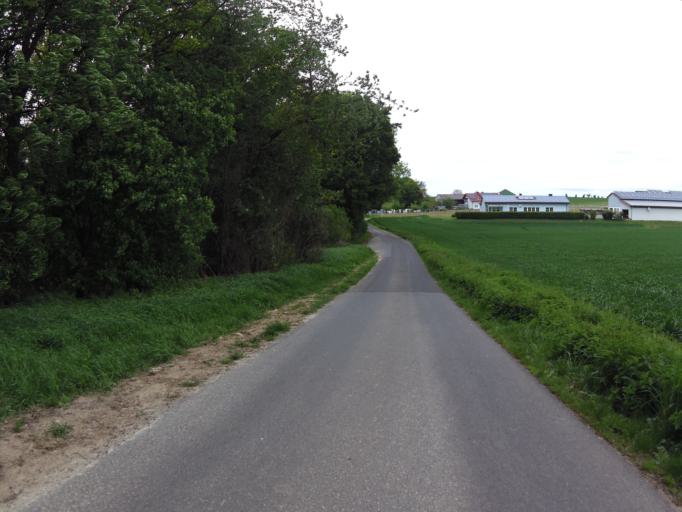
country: DE
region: Bavaria
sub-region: Regierungsbezirk Unterfranken
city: Oberpleichfeld
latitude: 49.8450
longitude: 10.0732
